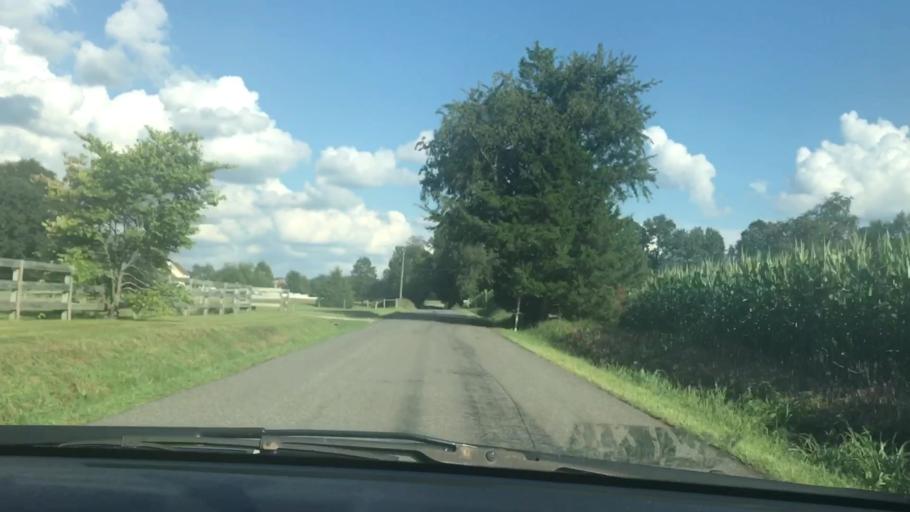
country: US
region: Virginia
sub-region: Henrico County
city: Wyndham
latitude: 37.6751
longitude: -77.7202
